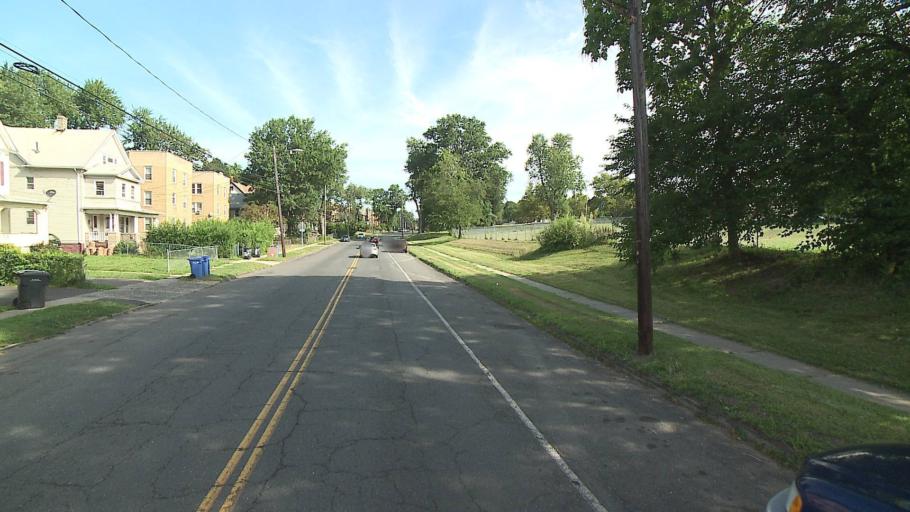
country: US
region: Connecticut
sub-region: Hartford County
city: Hartford
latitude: 41.7849
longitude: -72.6984
